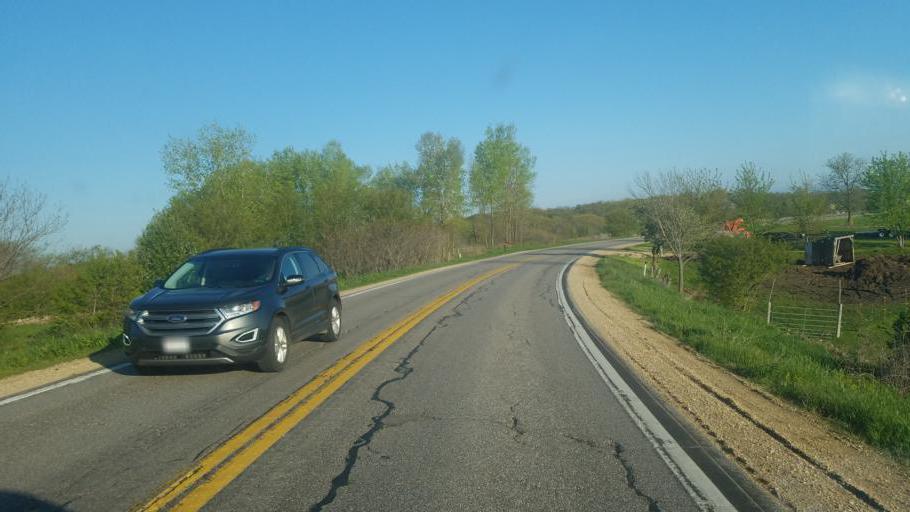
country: US
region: Wisconsin
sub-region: Vernon County
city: Hillsboro
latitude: 43.5934
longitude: -90.4952
